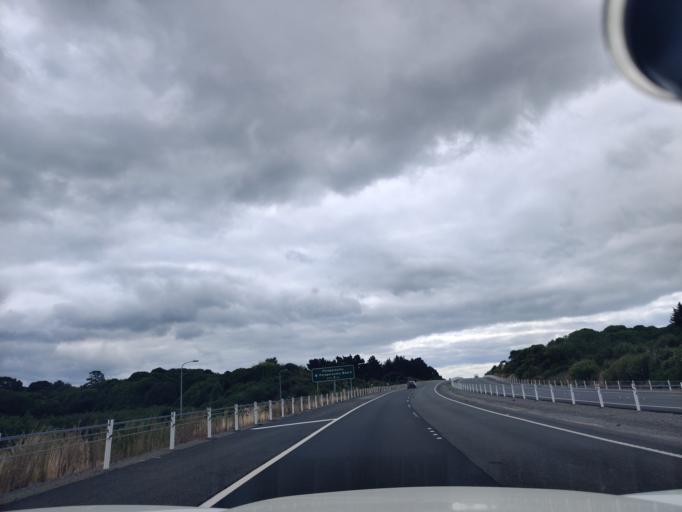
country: NZ
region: Wellington
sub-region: Kapiti Coast District
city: Paraparaumu
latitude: -40.9283
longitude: 174.9922
